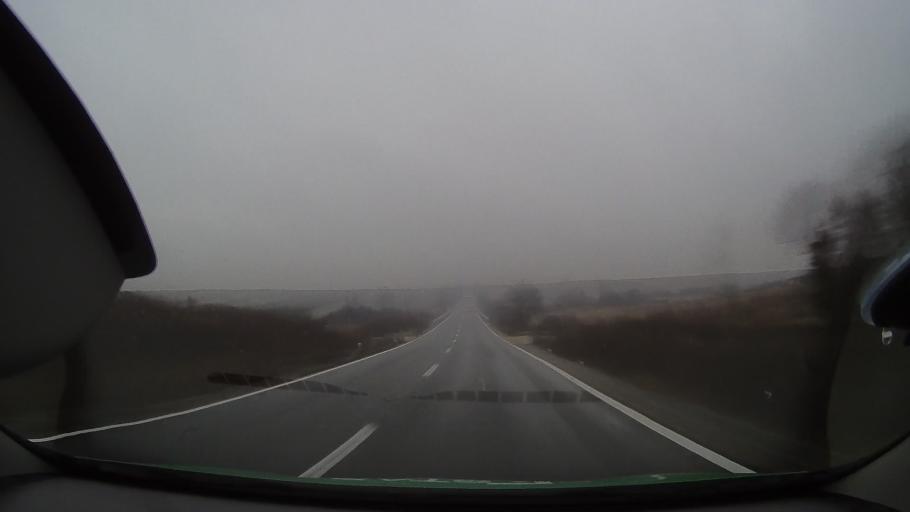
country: RO
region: Bihor
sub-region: Comuna Olcea
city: Olcea
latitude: 46.6803
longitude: 21.9660
